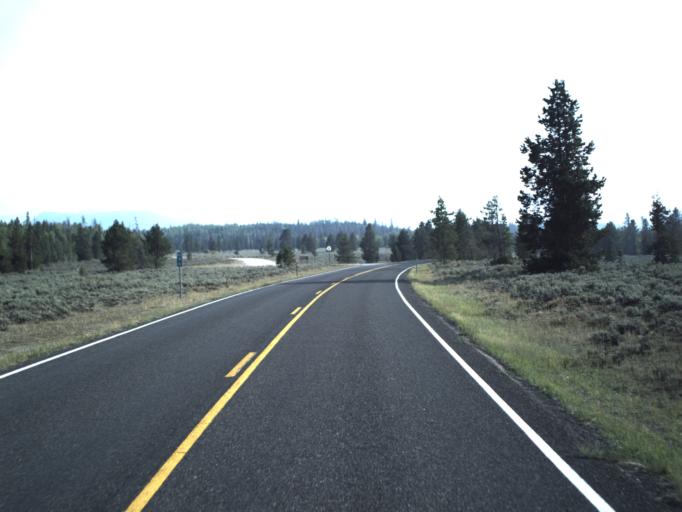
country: US
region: Wyoming
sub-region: Uinta County
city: Evanston
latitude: 40.8772
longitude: -110.8312
